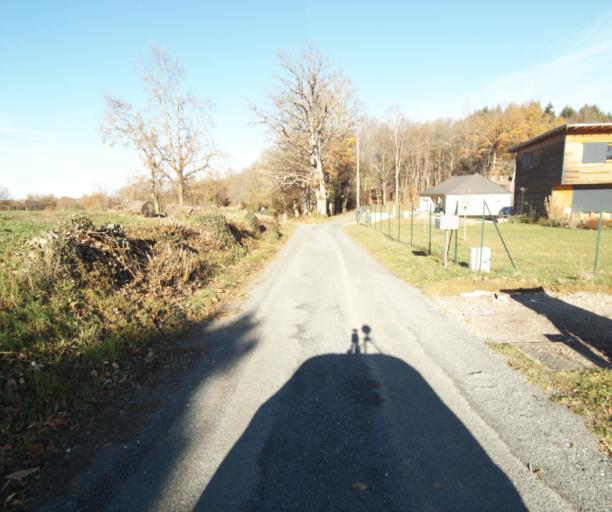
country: FR
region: Limousin
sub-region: Departement de la Correze
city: Sainte-Fortunade
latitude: 45.2144
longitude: 1.7793
